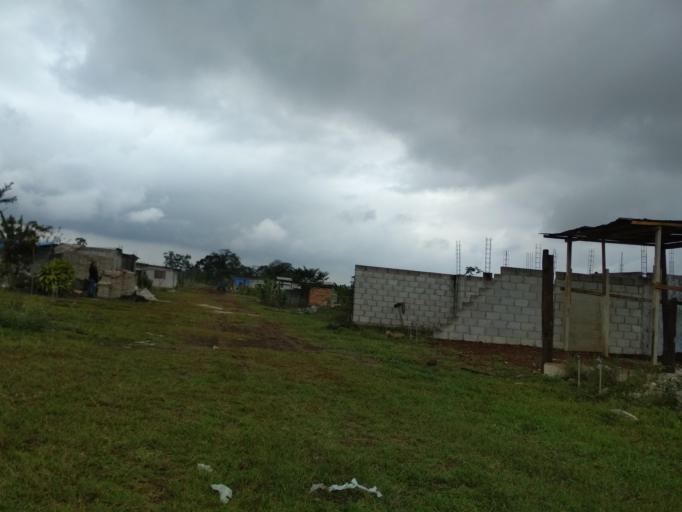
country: MX
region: Veracruz
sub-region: Cordoba
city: San Jose de Tapia
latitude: 18.8474
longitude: -96.9643
